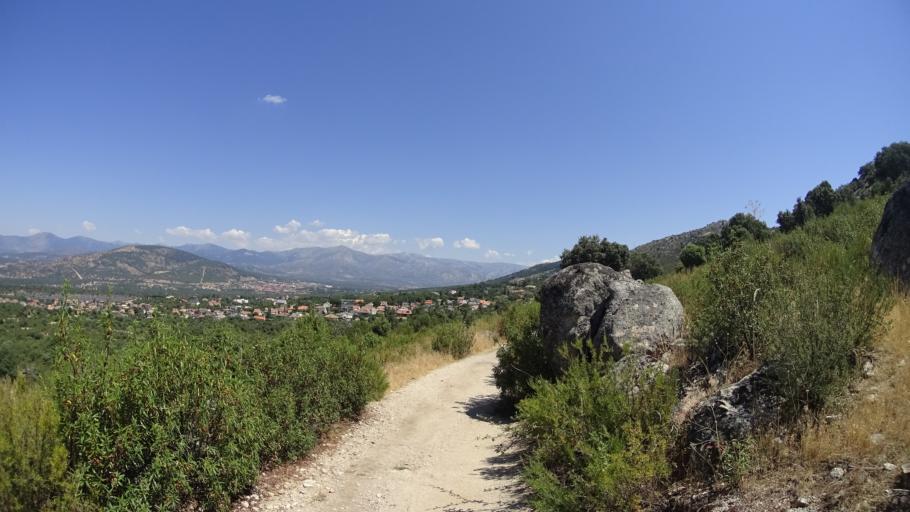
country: ES
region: Madrid
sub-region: Provincia de Madrid
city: Moralzarzal
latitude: 40.6414
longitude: -3.9651
